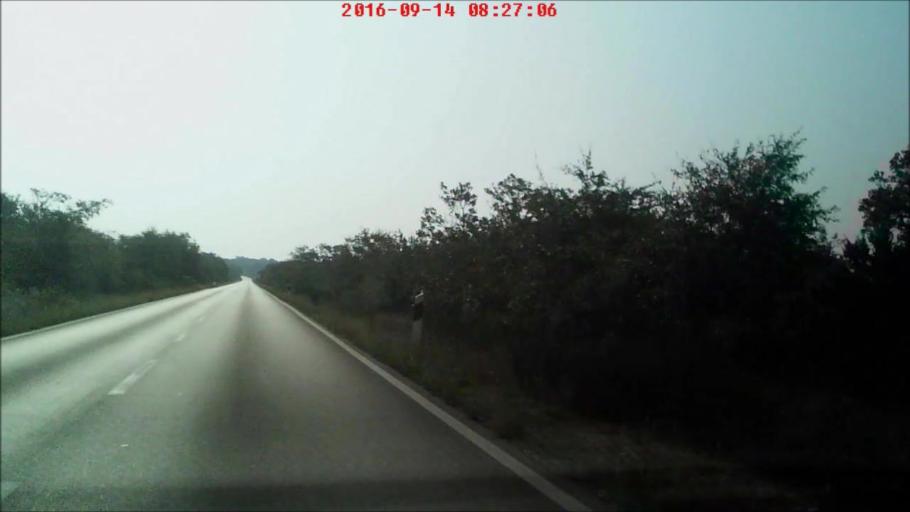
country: HR
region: Zadarska
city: Zadar
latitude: 44.1911
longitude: 15.2619
